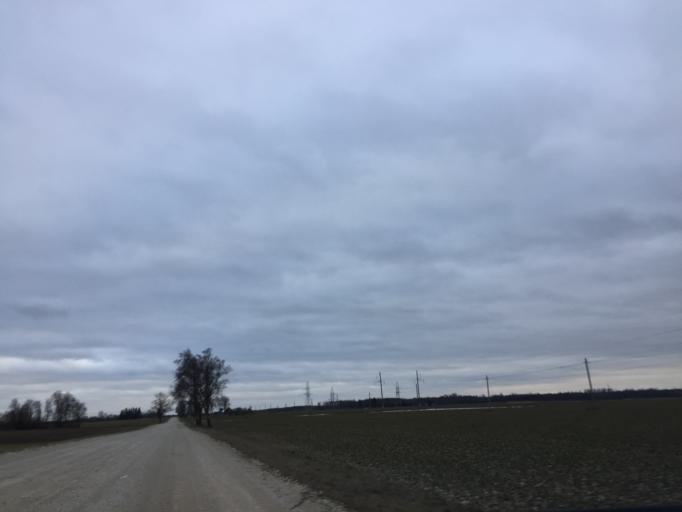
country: LT
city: Zagare
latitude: 56.3421
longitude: 23.2498
